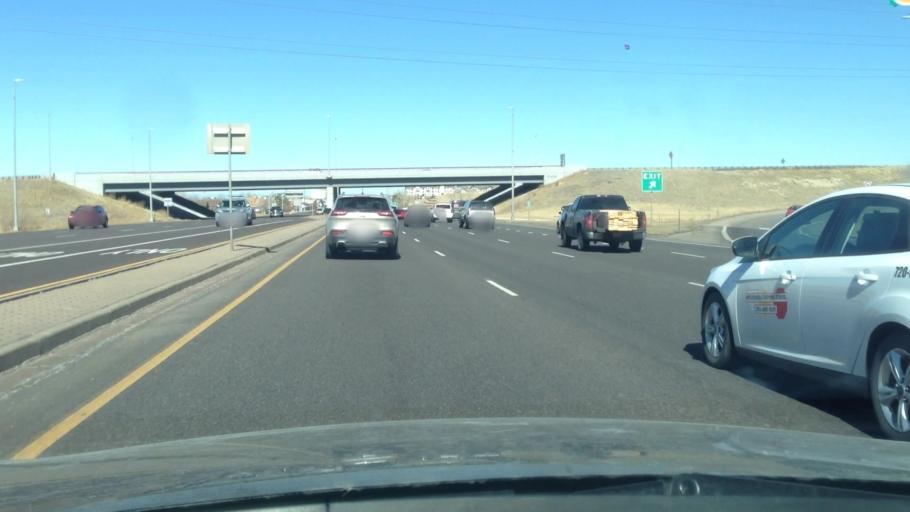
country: US
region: Colorado
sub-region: Douglas County
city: Stonegate
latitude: 39.5503
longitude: -104.7753
